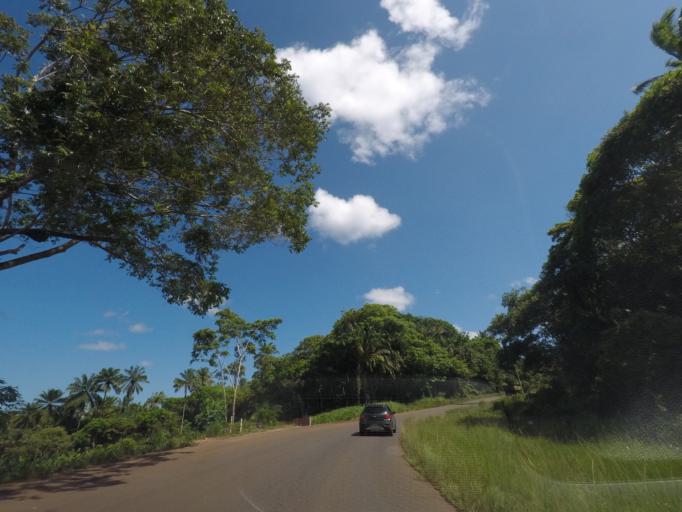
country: BR
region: Bahia
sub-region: Taperoa
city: Taperoa
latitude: -13.5857
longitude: -39.1056
